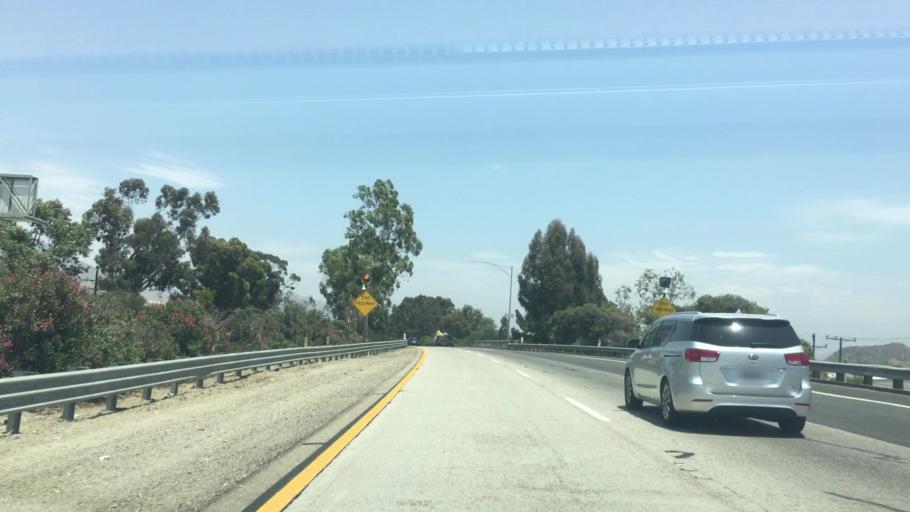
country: US
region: California
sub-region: Ventura County
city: Santa Paula
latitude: 34.3510
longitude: -119.0552
